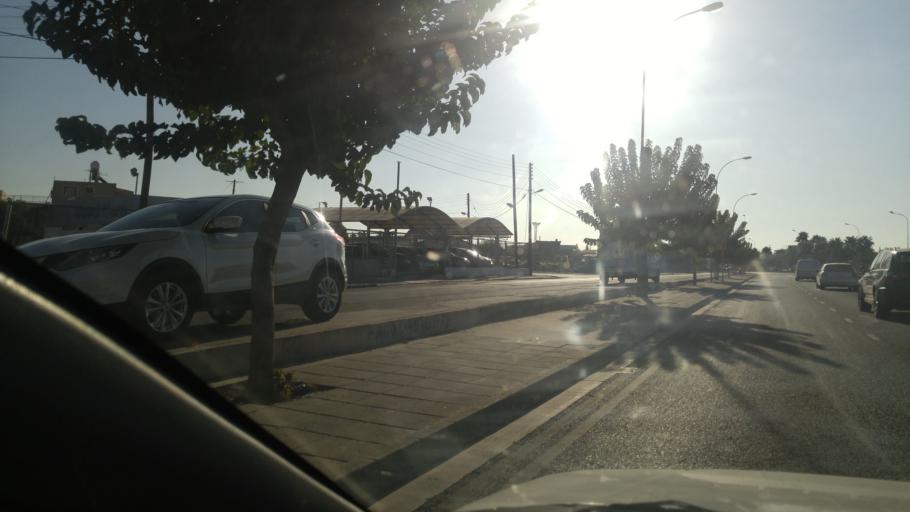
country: CY
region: Limassol
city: Pano Polemidia
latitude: 34.6780
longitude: 32.9971
